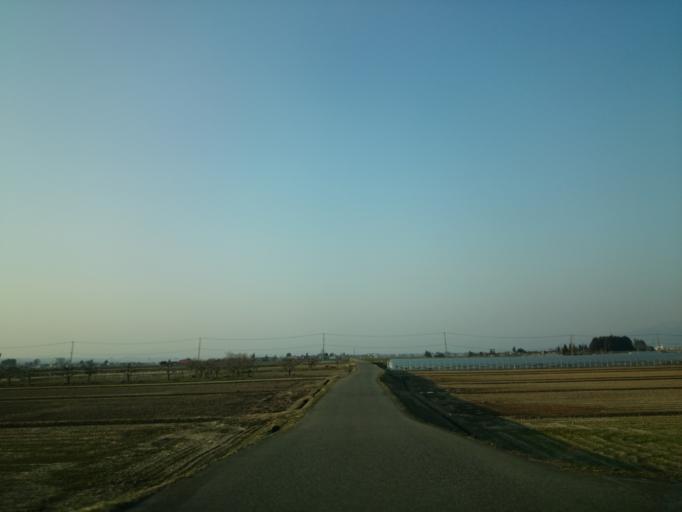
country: JP
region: Fukushima
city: Kitakata
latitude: 37.4446
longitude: 139.8577
